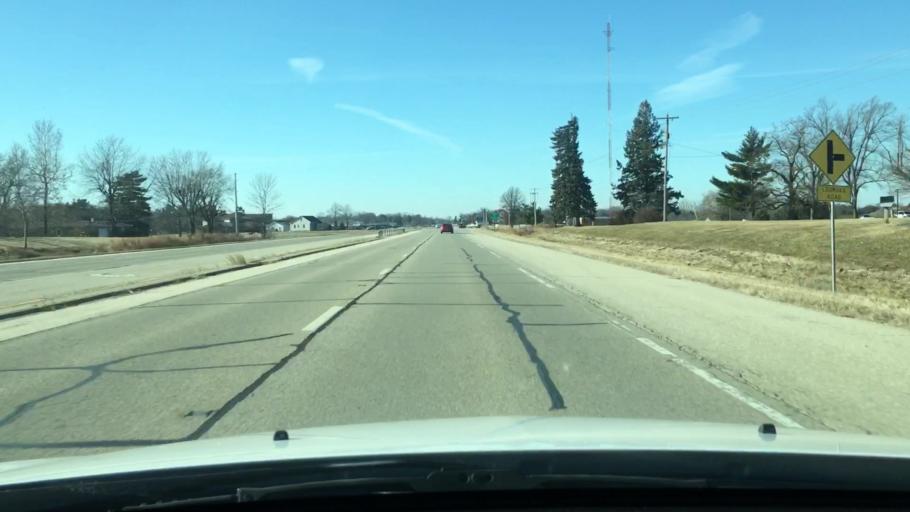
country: US
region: Illinois
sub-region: Woodford County
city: Germantown Hills
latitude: 40.7726
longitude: -89.4383
